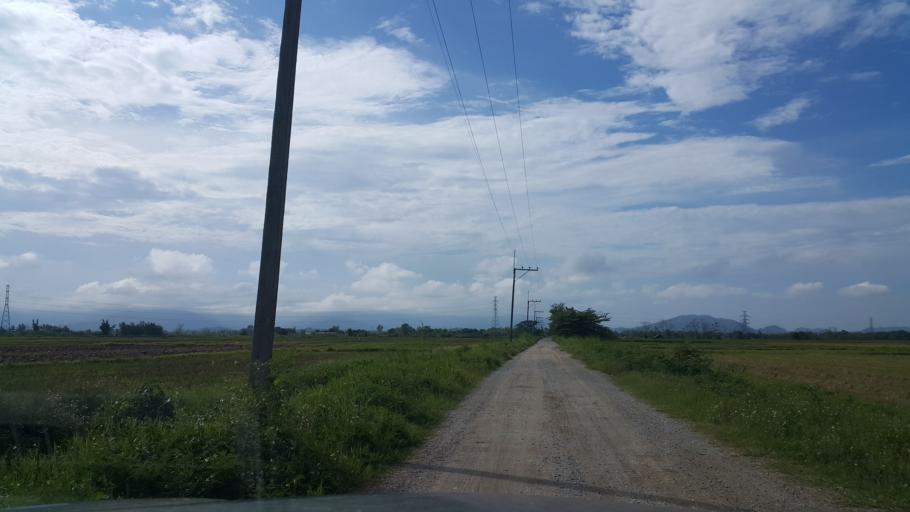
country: TH
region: Chiang Rai
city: Wiang Chai
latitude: 19.9549
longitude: 99.9291
